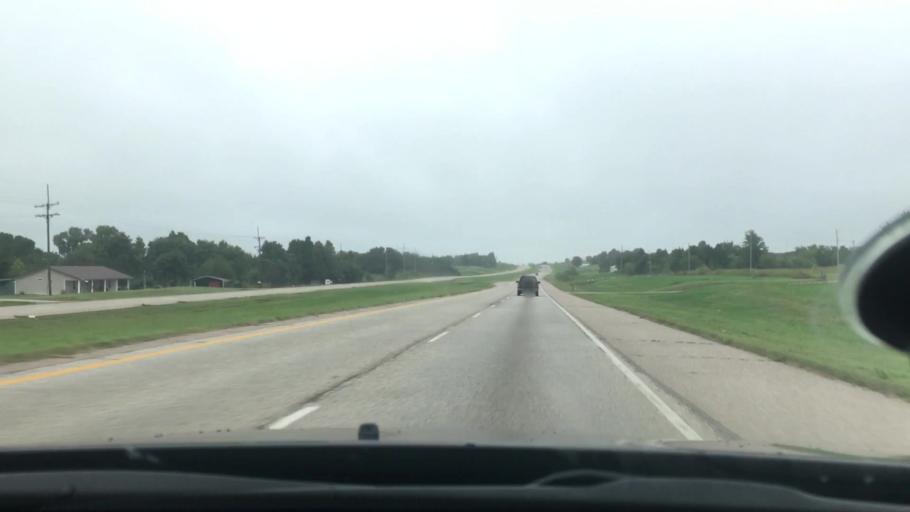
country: US
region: Oklahoma
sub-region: Seminole County
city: Seminole
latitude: 35.2948
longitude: -96.6708
